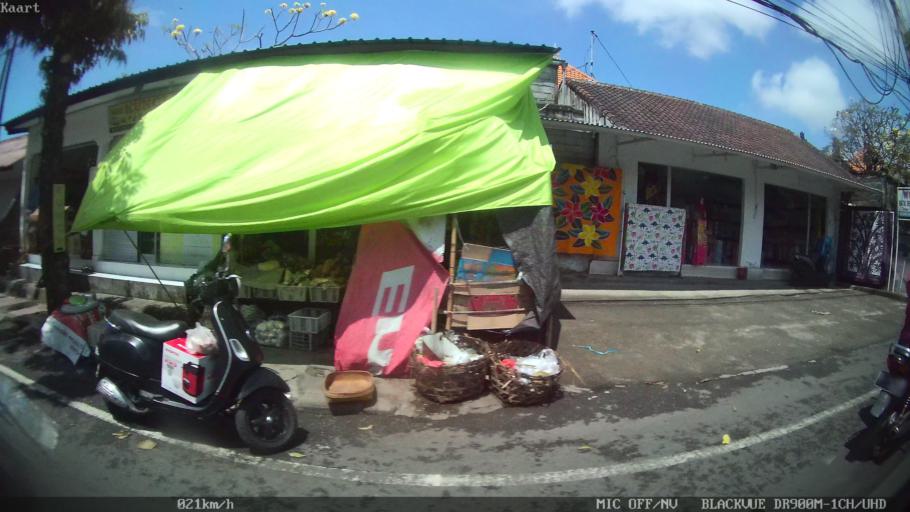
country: ID
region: Bali
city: Banjar Pasekan
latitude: -8.6030
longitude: 115.2815
